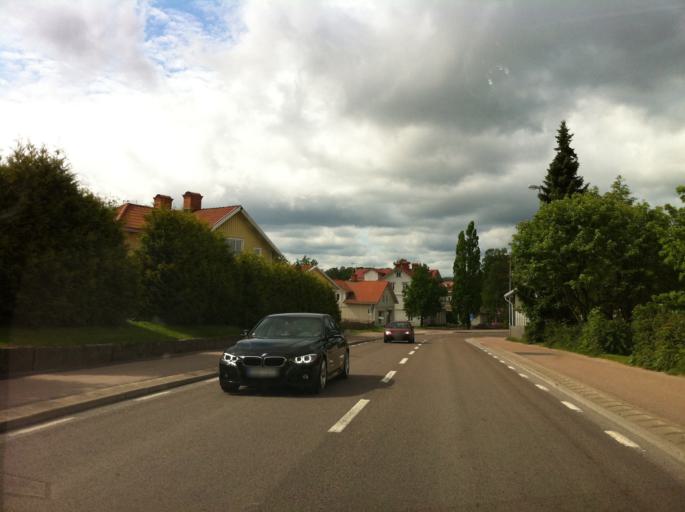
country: SE
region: Vaermland
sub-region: Sunne Kommun
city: Sunne
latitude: 59.8397
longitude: 13.1522
